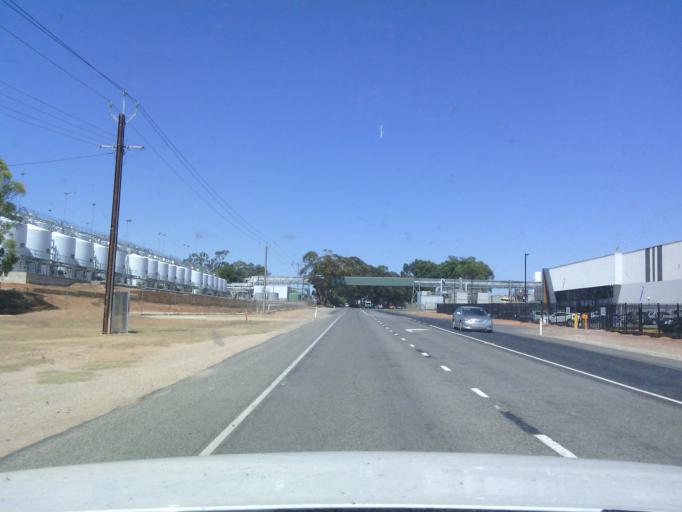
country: AU
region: South Australia
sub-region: Berri and Barmera
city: Monash
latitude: -34.2785
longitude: 140.5412
